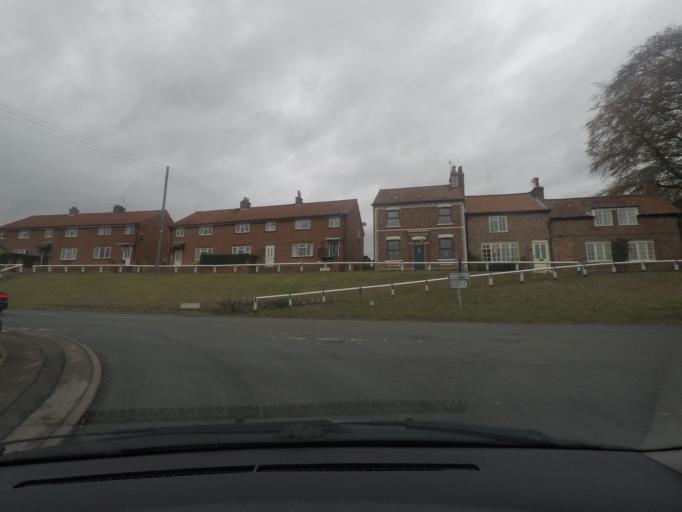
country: GB
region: England
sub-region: North Yorkshire
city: Easingwold
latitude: 54.1027
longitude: -1.1107
